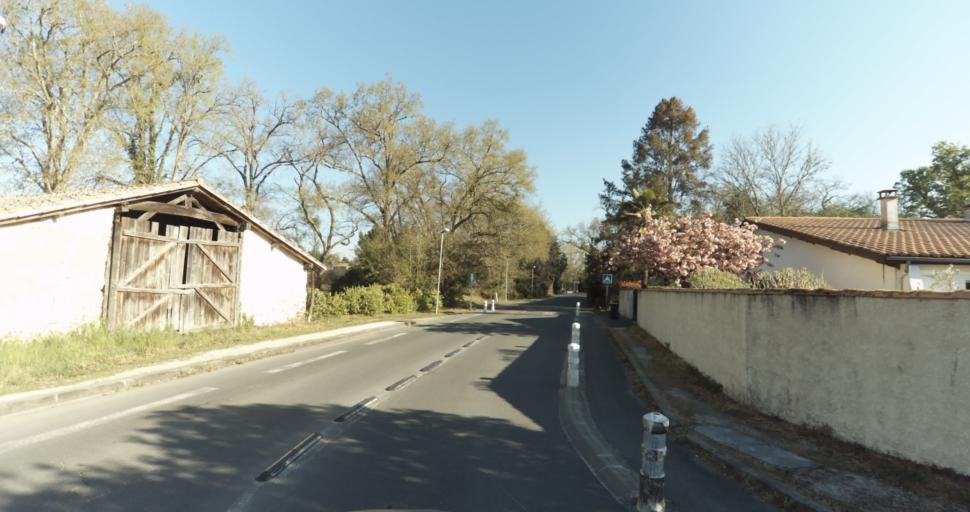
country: FR
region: Aquitaine
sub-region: Departement de la Gironde
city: Martignas-sur-Jalle
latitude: 44.8048
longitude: -0.7952
